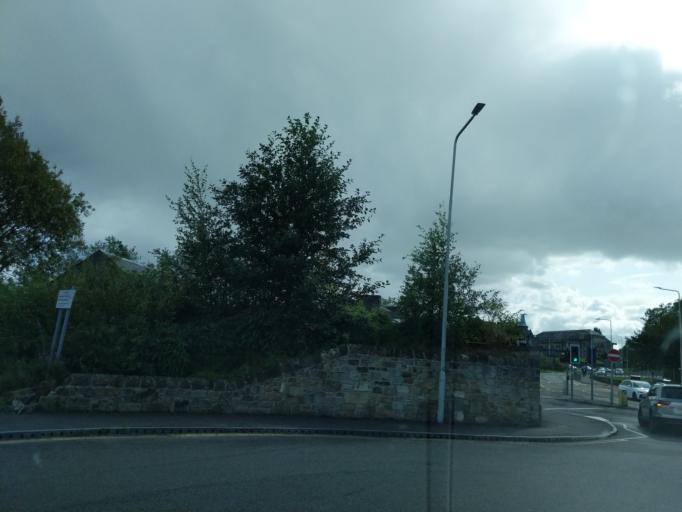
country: GB
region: Scotland
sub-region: Fife
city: Dunfermline
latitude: 56.0742
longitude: -3.4518
